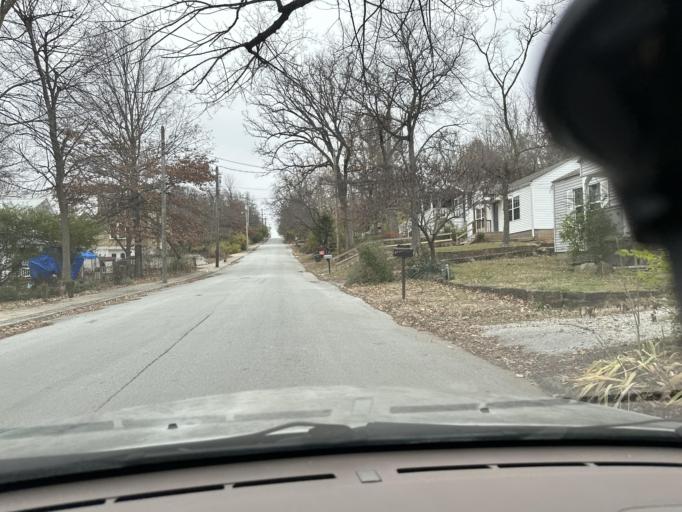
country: US
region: Arkansas
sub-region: Washington County
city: Fayetteville
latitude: 36.0597
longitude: -94.1631
